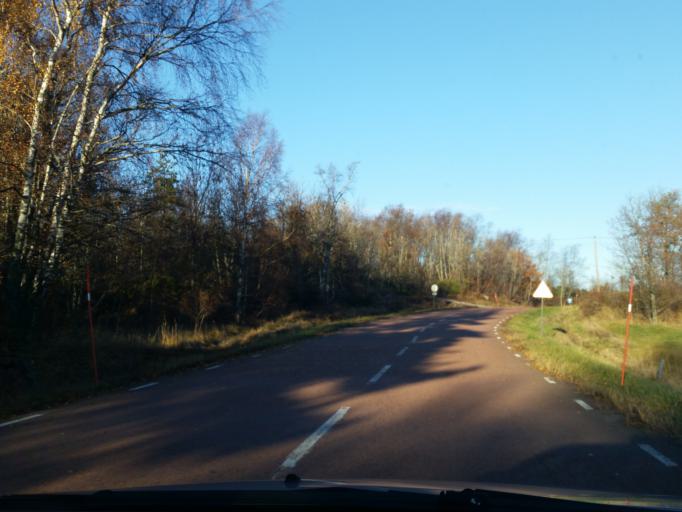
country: AX
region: Alands skaergard
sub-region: Braendoe
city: Braendoe
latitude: 60.3625
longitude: 21.0681
